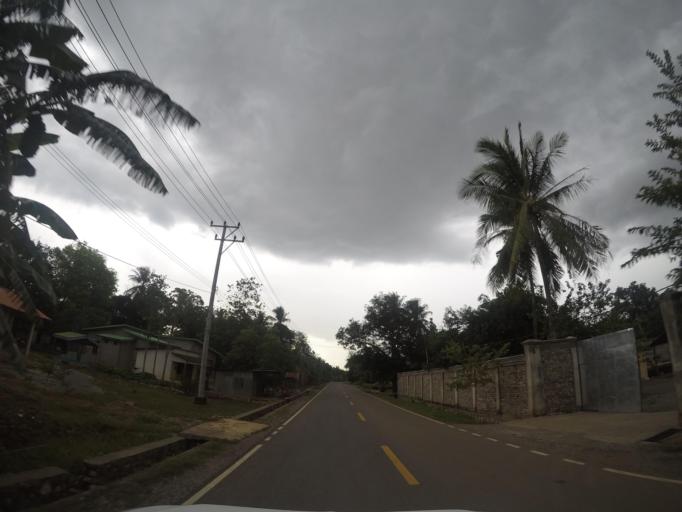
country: TL
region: Bobonaro
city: Maliana
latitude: -8.9614
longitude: 125.2154
